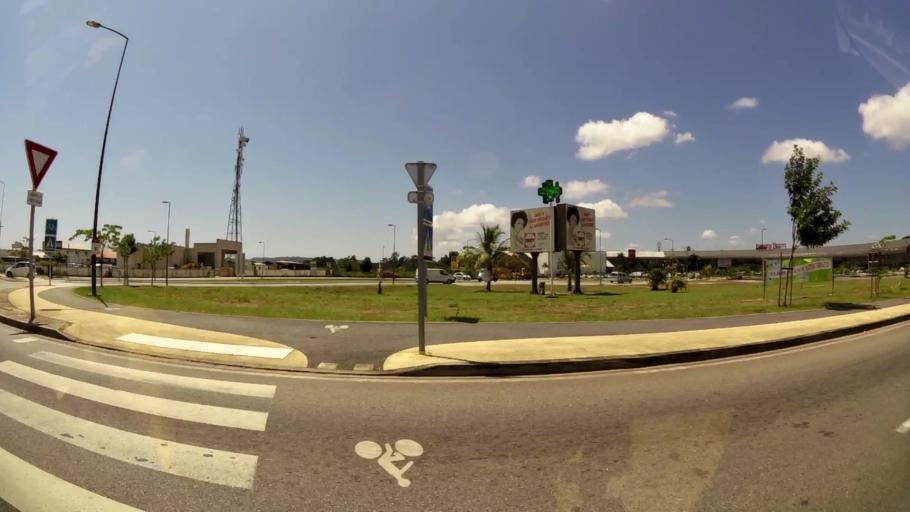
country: GF
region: Guyane
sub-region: Guyane
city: Cayenne
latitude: 4.8904
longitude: -52.3332
